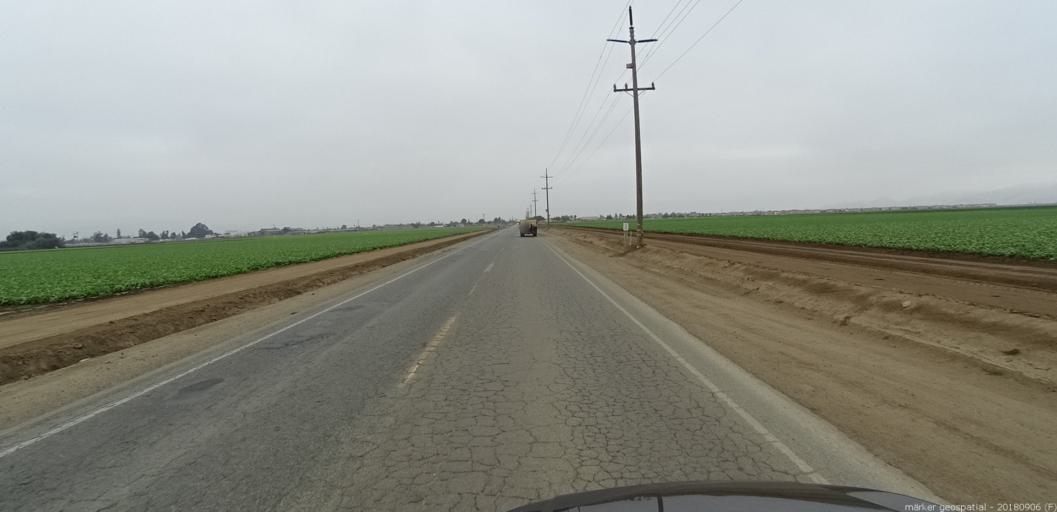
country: US
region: California
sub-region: Monterey County
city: Salinas
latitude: 36.6658
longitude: -121.5948
